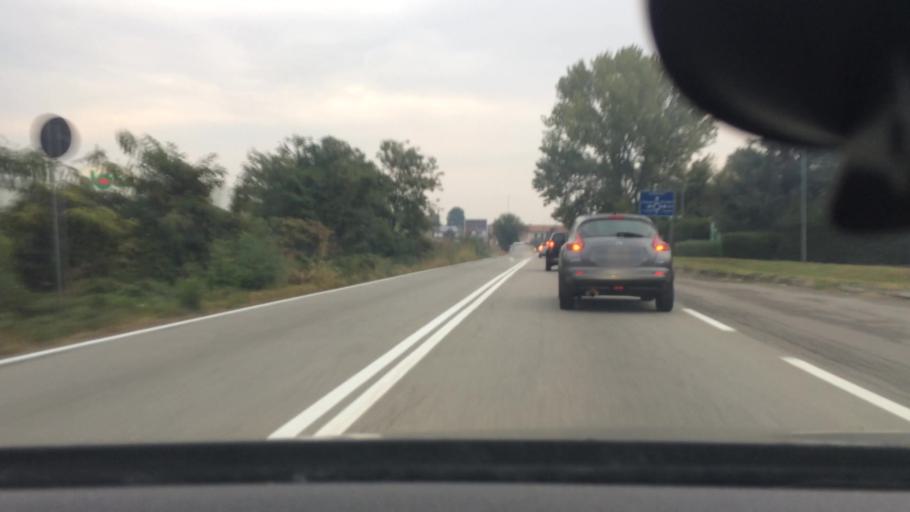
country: IT
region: Lombardy
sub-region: Citta metropolitana di Milano
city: Pogliano Milanese
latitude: 45.5400
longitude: 9.0112
